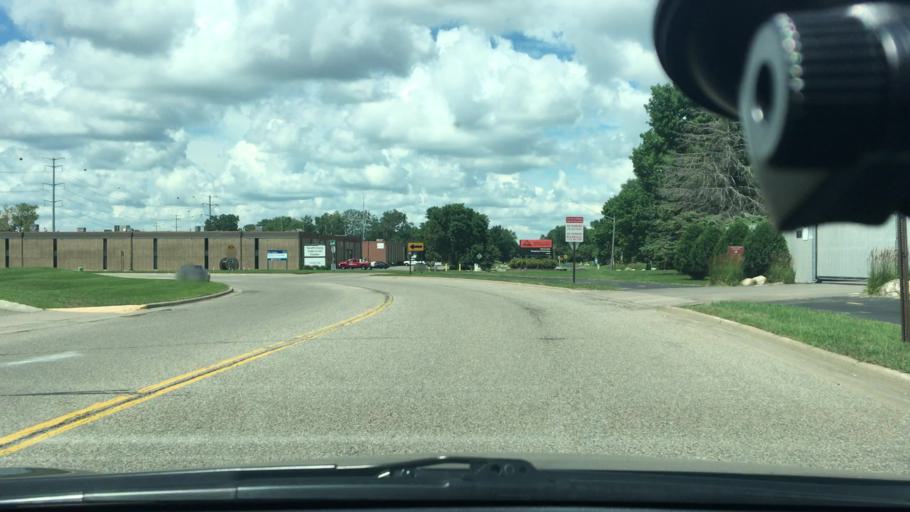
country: US
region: Minnesota
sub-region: Hennepin County
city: New Hope
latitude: 44.9933
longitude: -93.4033
